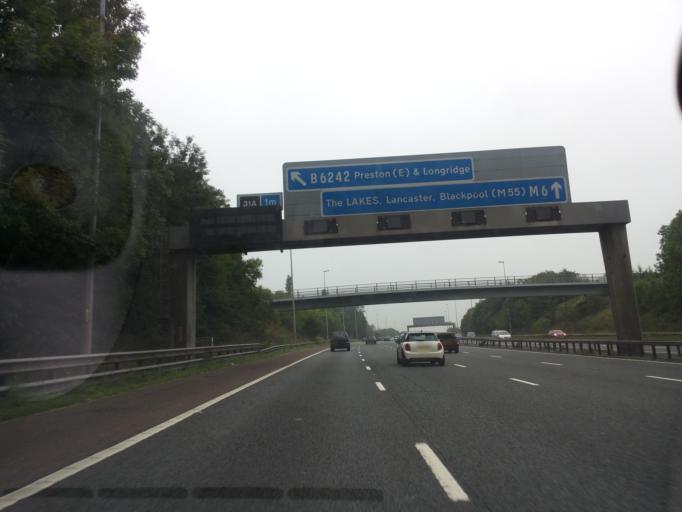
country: GB
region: England
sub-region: Lancashire
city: Goosnargh
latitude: 53.7759
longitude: -2.6442
